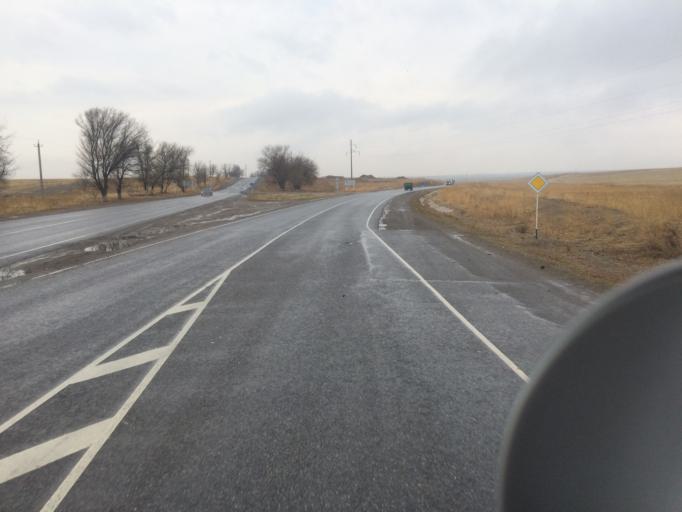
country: KZ
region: Zhambyl
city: Georgiyevka
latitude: 43.0394
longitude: 74.7643
